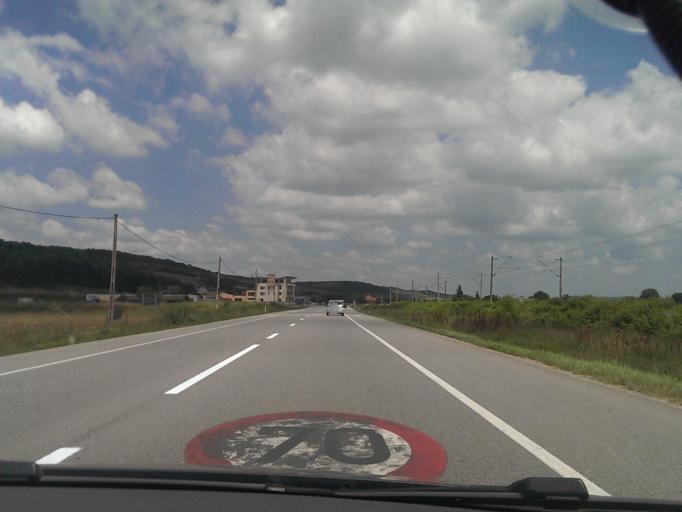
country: RO
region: Cluj
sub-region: Comuna Apahida
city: Apahida
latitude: 46.8341
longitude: 23.7462
